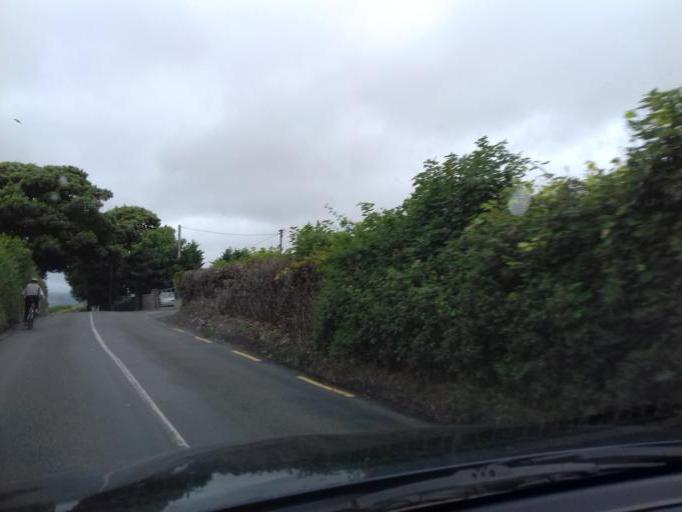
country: IE
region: Leinster
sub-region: County Carlow
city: Bagenalstown
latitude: 52.7189
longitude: -6.9647
